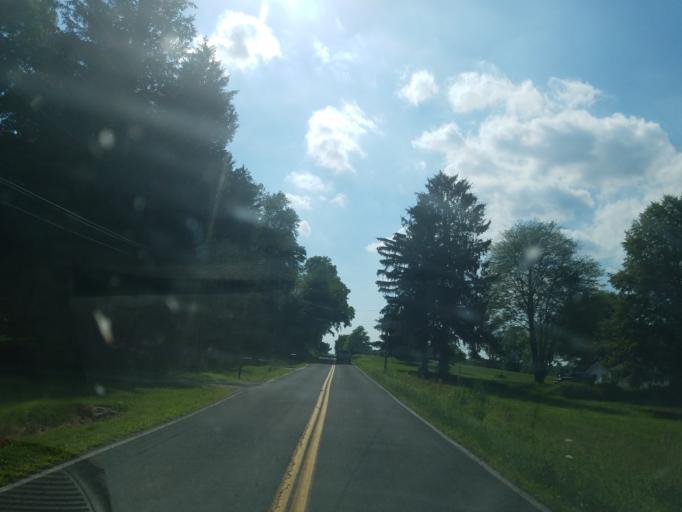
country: US
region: Ohio
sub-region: Portage County
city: Brimfield
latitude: 41.0502
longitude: -81.3114
